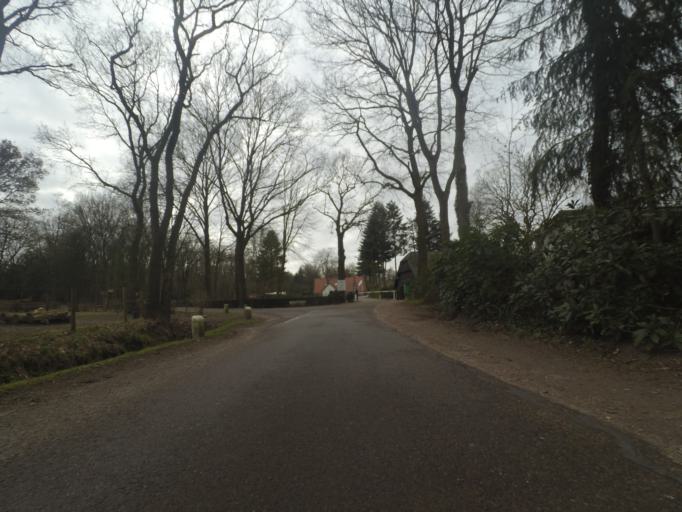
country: NL
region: Utrecht
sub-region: Gemeente Utrechtse Heuvelrug
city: Overberg
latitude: 52.0288
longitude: 5.4977
